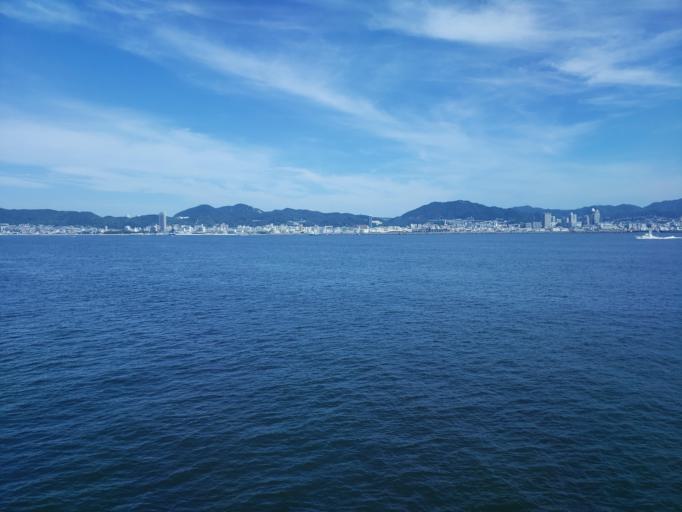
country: JP
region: Hyogo
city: Kobe
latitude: 34.6269
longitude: 135.1513
